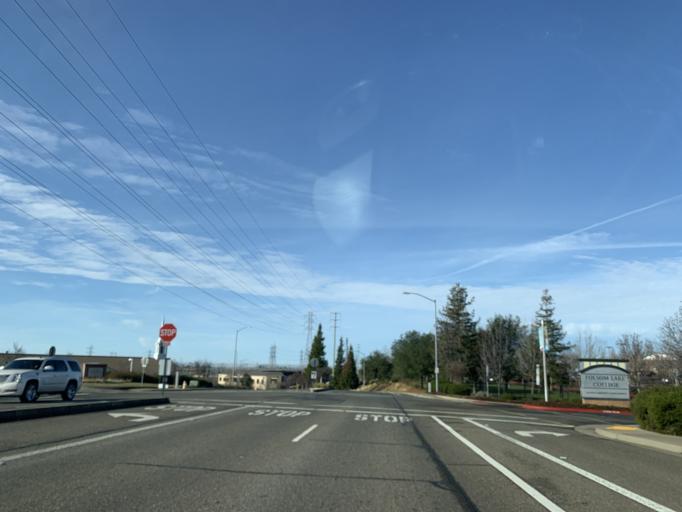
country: US
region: California
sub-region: El Dorado County
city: El Dorado Hills
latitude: 38.6596
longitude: -121.1229
